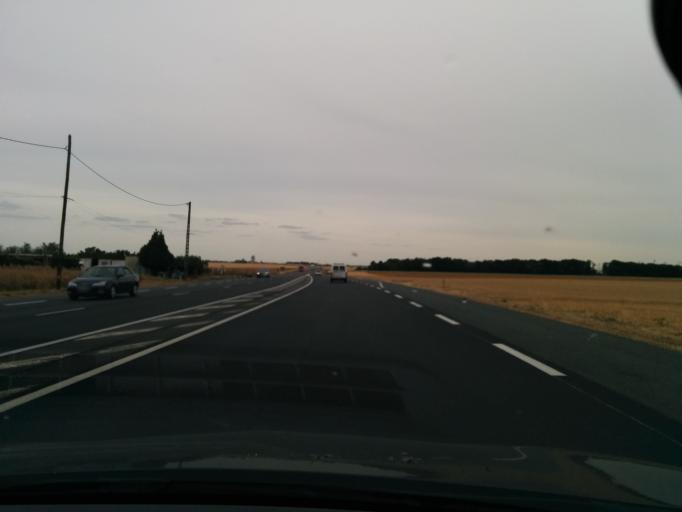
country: FR
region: Ile-de-France
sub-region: Departement de l'Essonne
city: Angerville
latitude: 48.2893
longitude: 1.9817
